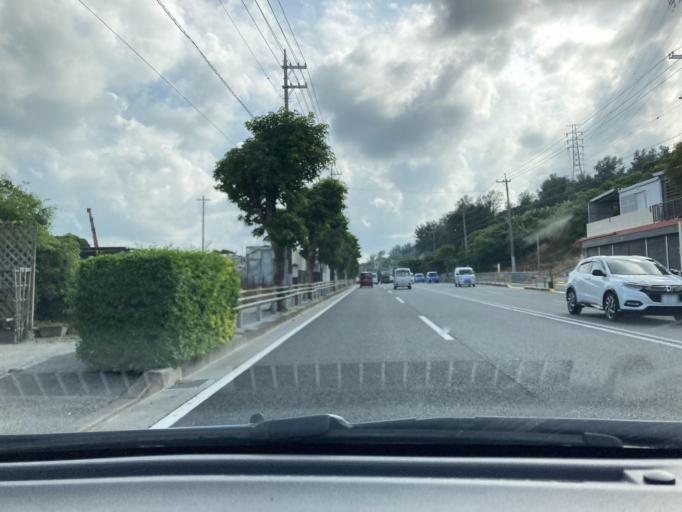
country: JP
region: Okinawa
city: Ginowan
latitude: 26.2522
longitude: 127.7836
